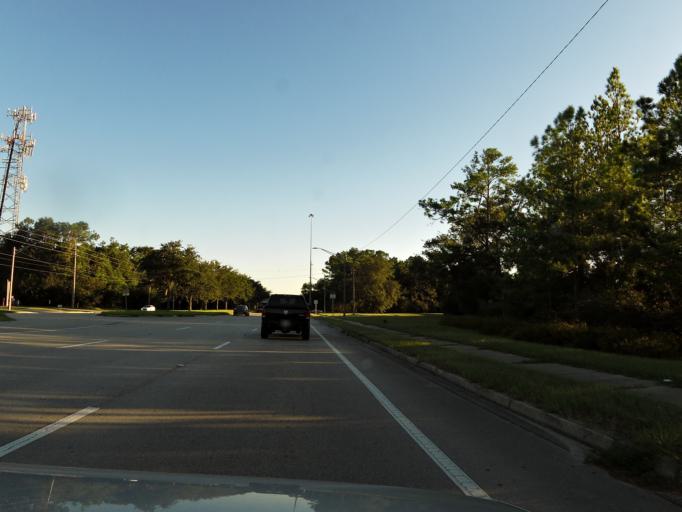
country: US
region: Florida
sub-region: Saint Johns County
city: Ponte Vedra Beach
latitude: 30.2600
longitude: -81.4373
